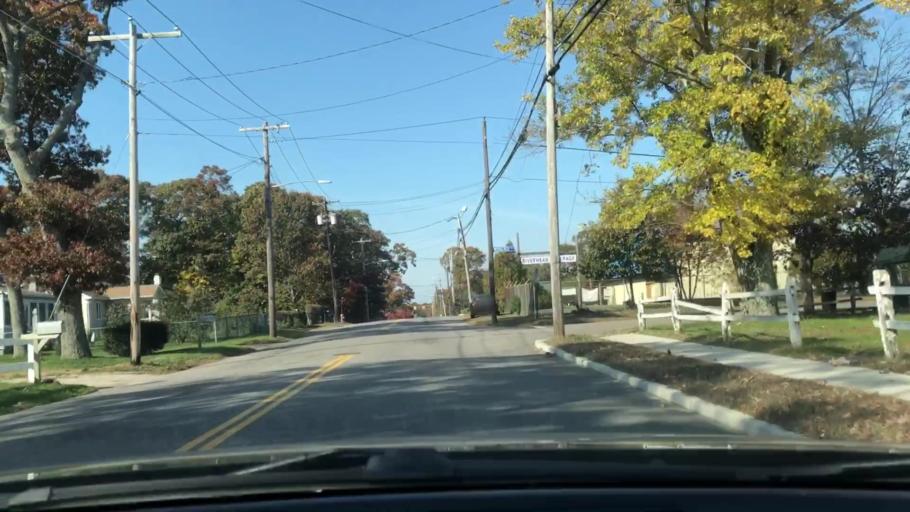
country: US
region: New York
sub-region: Suffolk County
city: Riverhead
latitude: 40.9272
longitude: -72.6815
